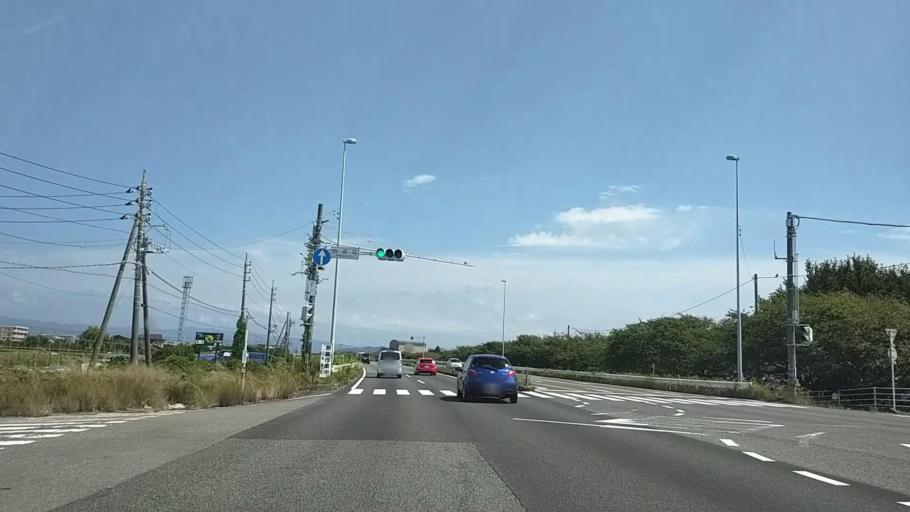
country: JP
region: Shizuoka
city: Numazu
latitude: 35.1315
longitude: 138.7893
